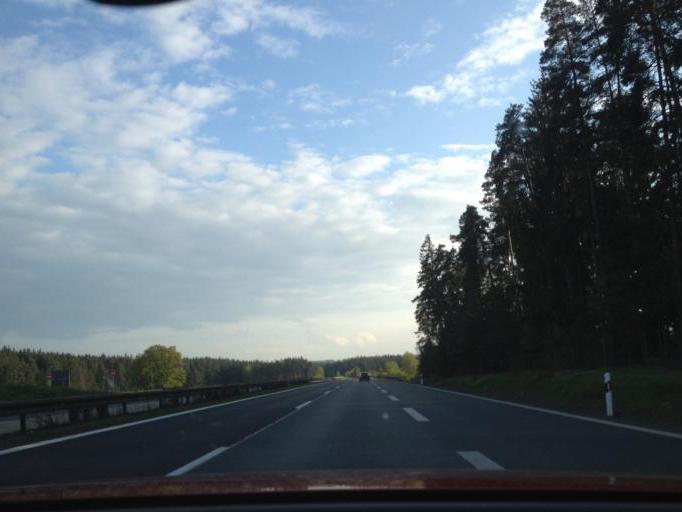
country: DE
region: Bavaria
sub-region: Upper Palatinate
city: Berg
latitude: 49.8367
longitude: 12.1715
